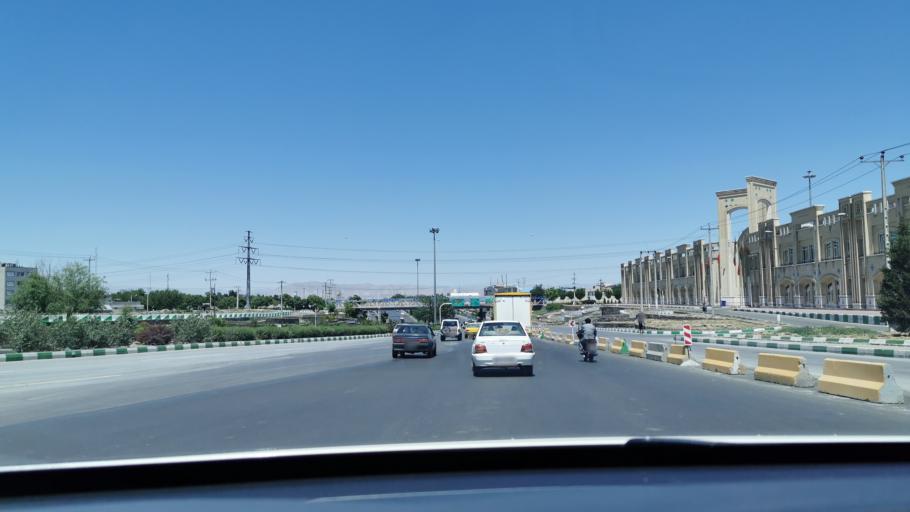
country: IR
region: Razavi Khorasan
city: Mashhad
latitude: 36.2611
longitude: 59.6492
